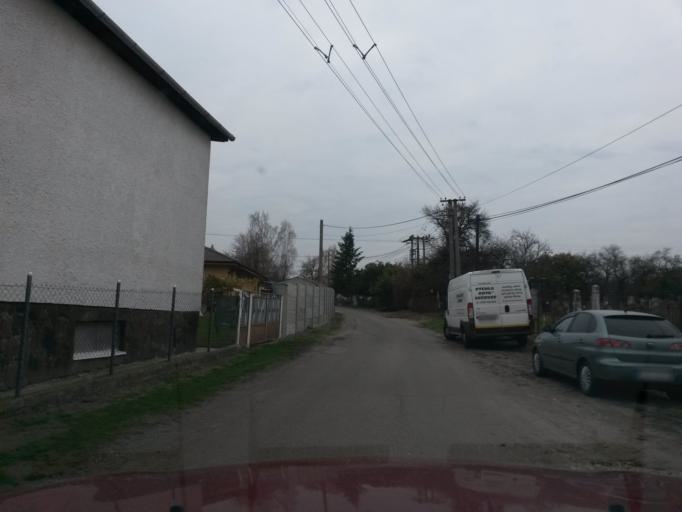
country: SK
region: Kosicky
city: Secovce
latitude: 48.7056
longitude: 21.6539
